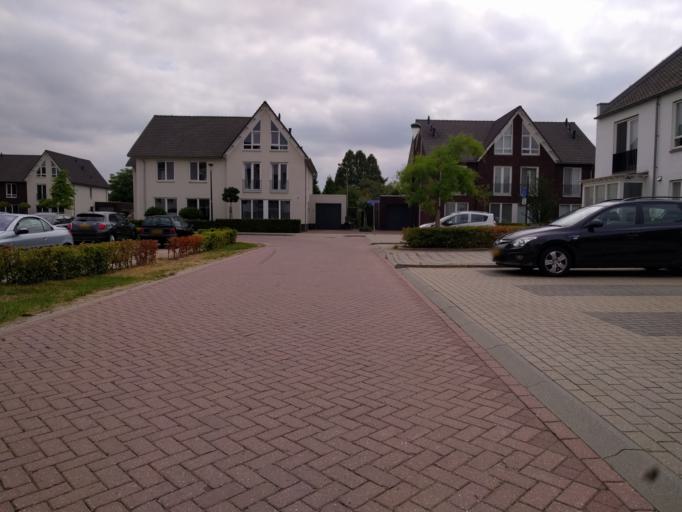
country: NL
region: Gelderland
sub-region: Gemeente Nijmegen
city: Nijmegen
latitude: 51.8657
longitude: 5.8649
